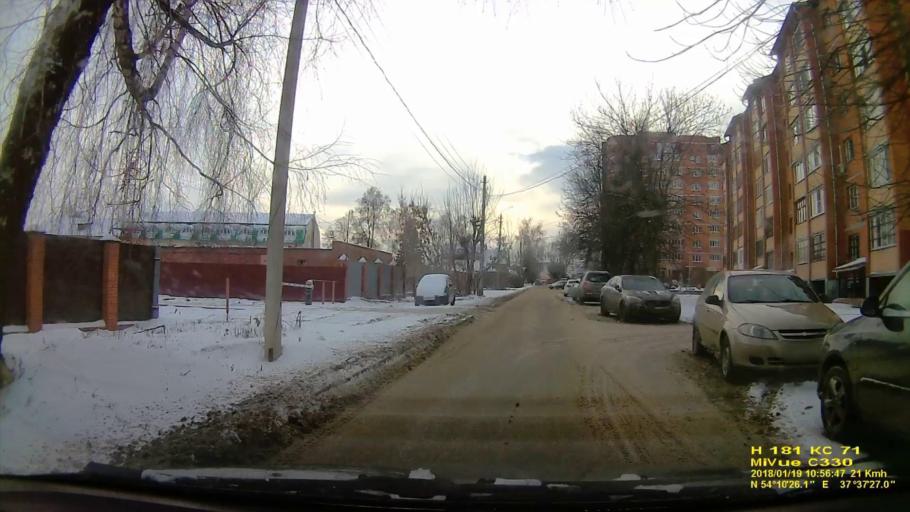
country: RU
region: Tula
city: Tula
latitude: 54.1738
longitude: 37.6243
